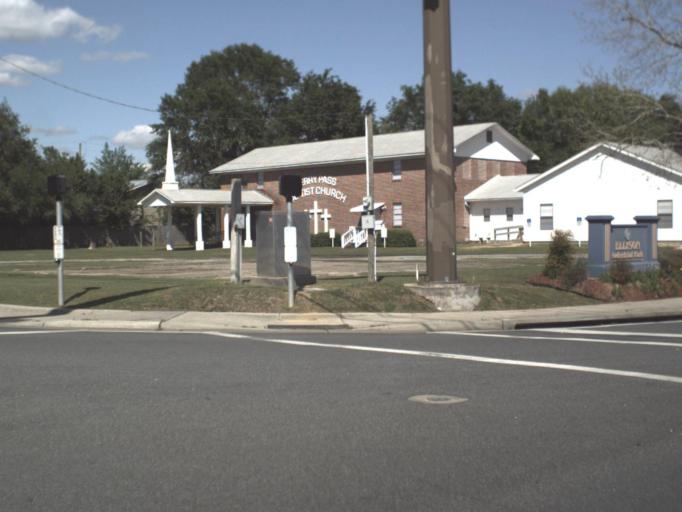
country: US
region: Florida
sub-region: Escambia County
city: Ferry Pass
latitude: 30.5297
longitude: -87.2083
